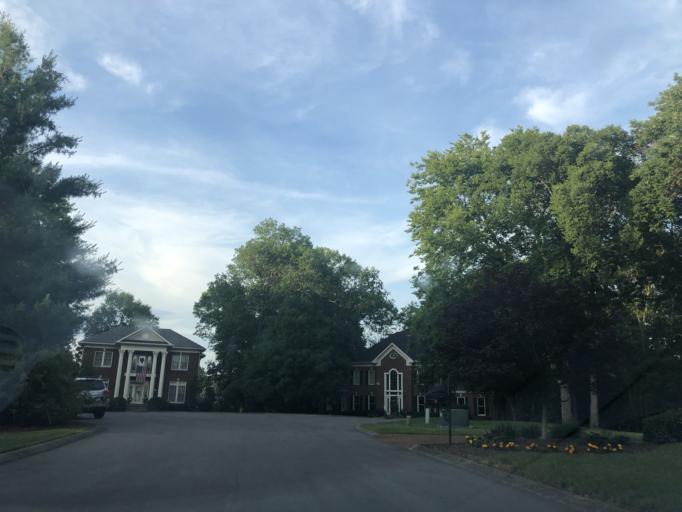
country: US
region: Tennessee
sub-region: Davidson County
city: Belle Meade
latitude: 36.0519
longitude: -86.9218
